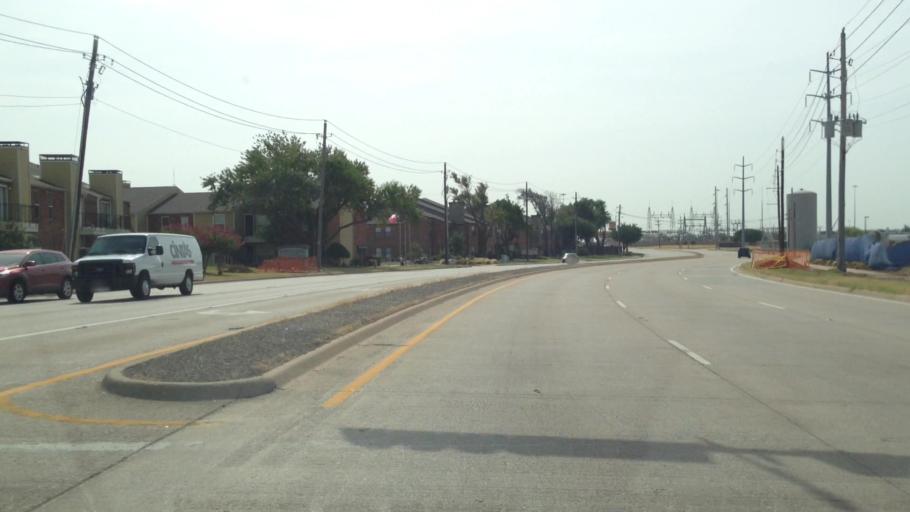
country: US
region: Texas
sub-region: Denton County
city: Lewisville
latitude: 33.0048
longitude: -97.0018
